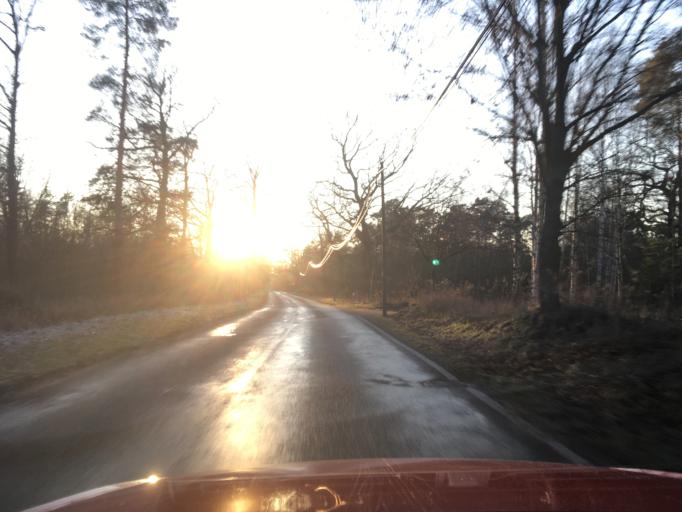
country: DE
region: Saxony-Anhalt
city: Rosslau
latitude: 51.9019
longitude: 12.2770
